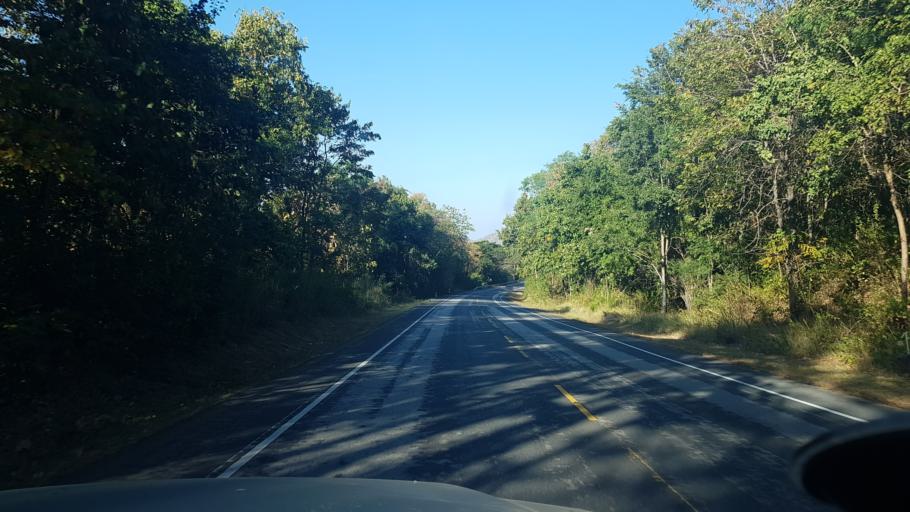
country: TH
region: Phetchabun
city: Lom Sak
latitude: 16.7394
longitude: 101.4161
